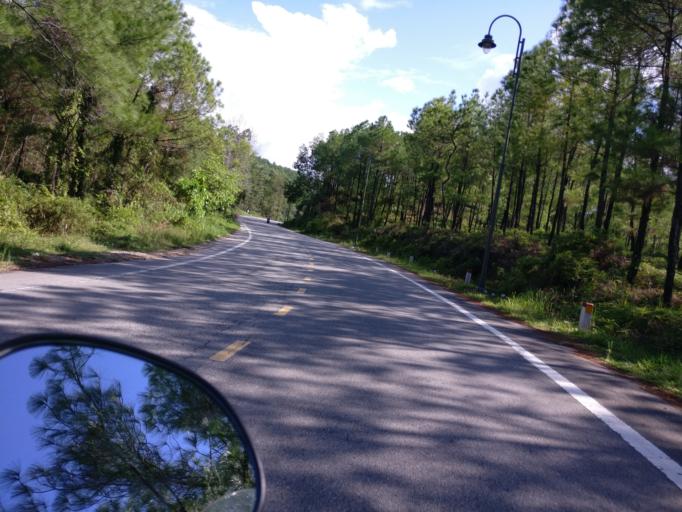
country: VN
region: Thua Thien-Hue
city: Hue
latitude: 16.4046
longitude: 107.5897
